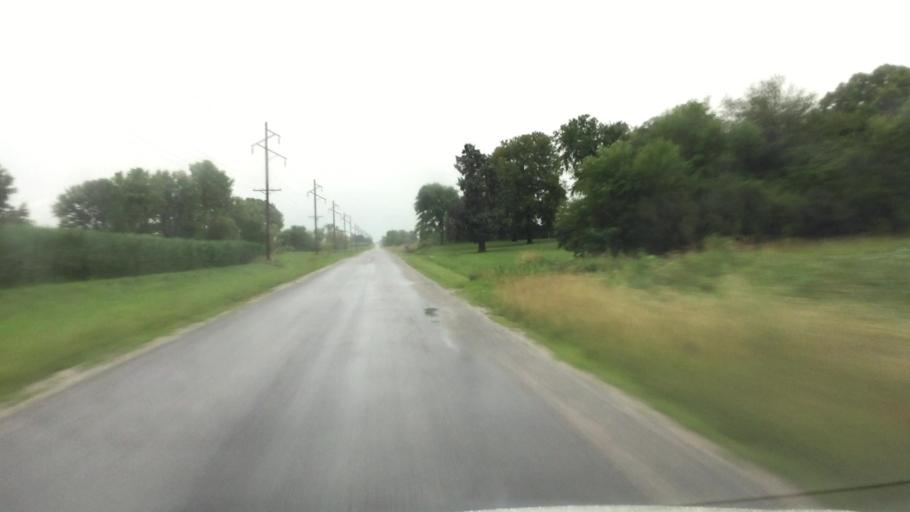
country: US
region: Illinois
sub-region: Hancock County
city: Hamilton
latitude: 40.4450
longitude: -91.2711
